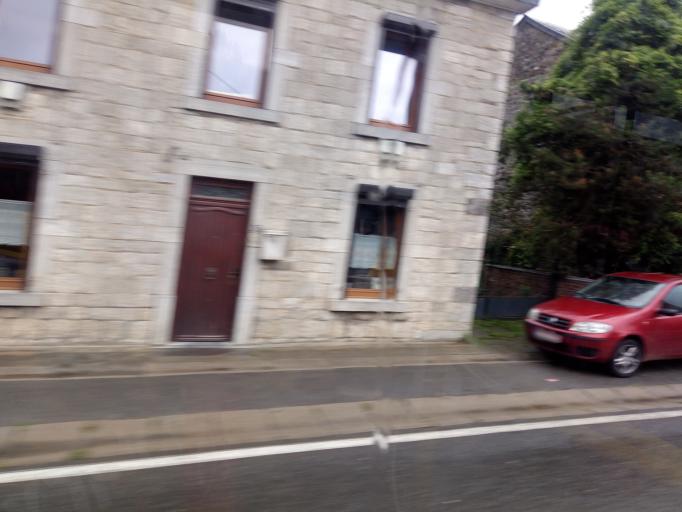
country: BE
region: Wallonia
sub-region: Province du Luxembourg
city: Hotton
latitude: 50.2580
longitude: 5.4723
